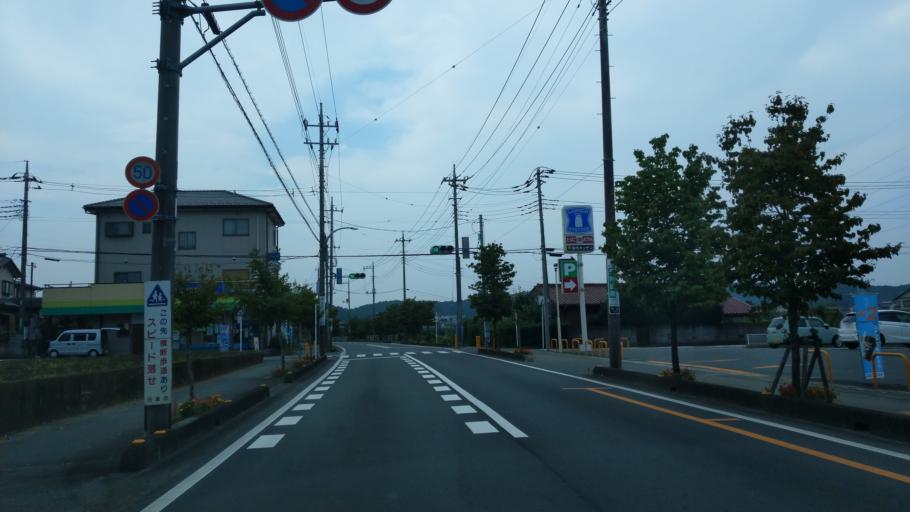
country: JP
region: Saitama
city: Hanno
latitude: 35.8963
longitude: 139.3321
